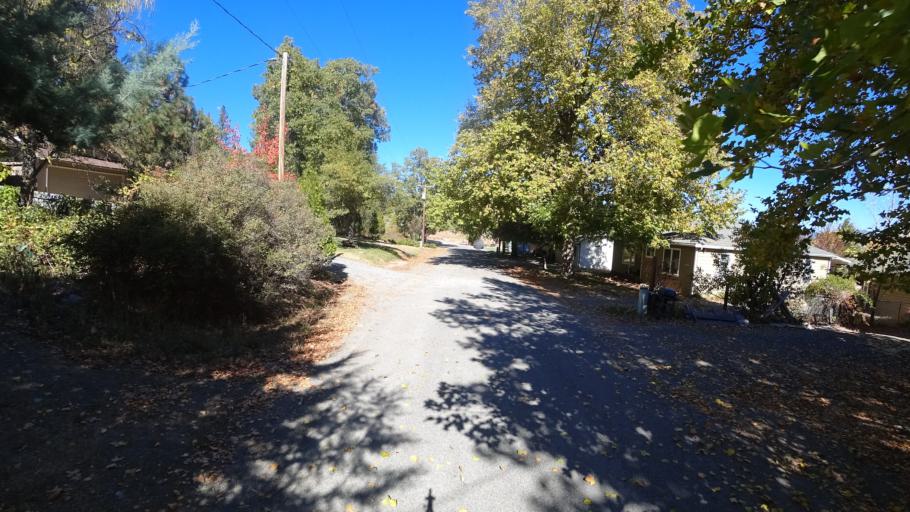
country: US
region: California
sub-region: Siskiyou County
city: Yreka
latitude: 41.4577
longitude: -122.9015
